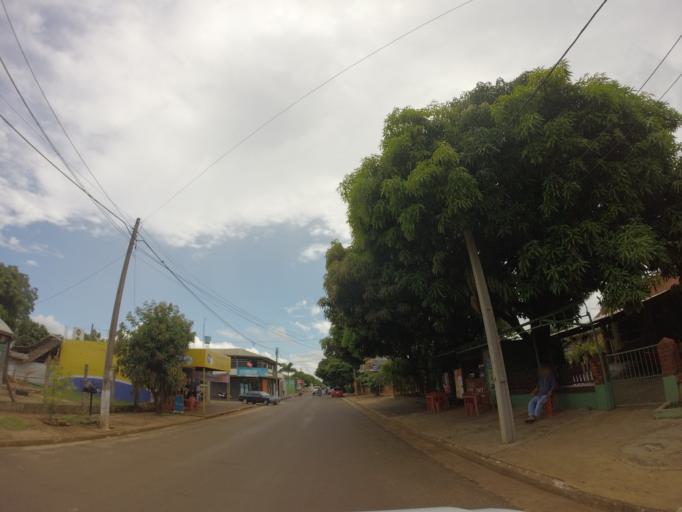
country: PY
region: Alto Parana
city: Ciudad del Este
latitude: -25.4131
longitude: -54.6270
